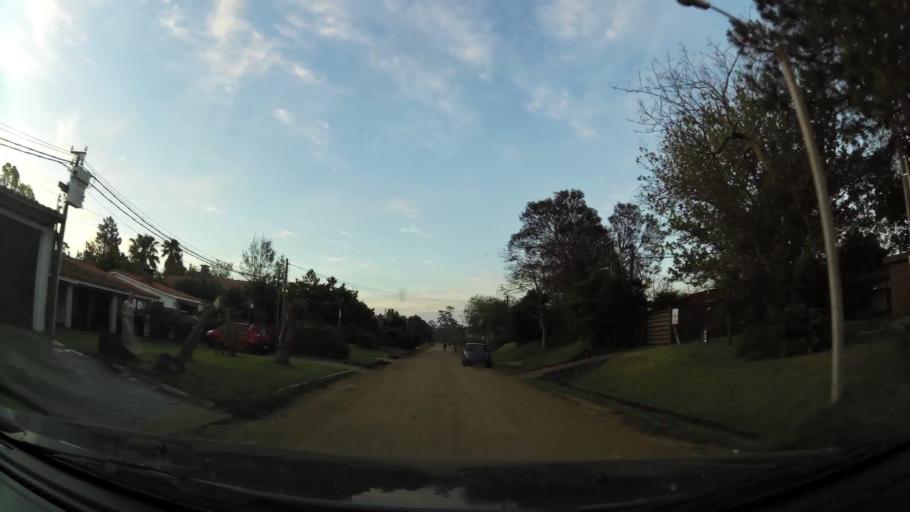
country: UY
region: Canelones
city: Atlantida
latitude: -34.7755
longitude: -55.7470
